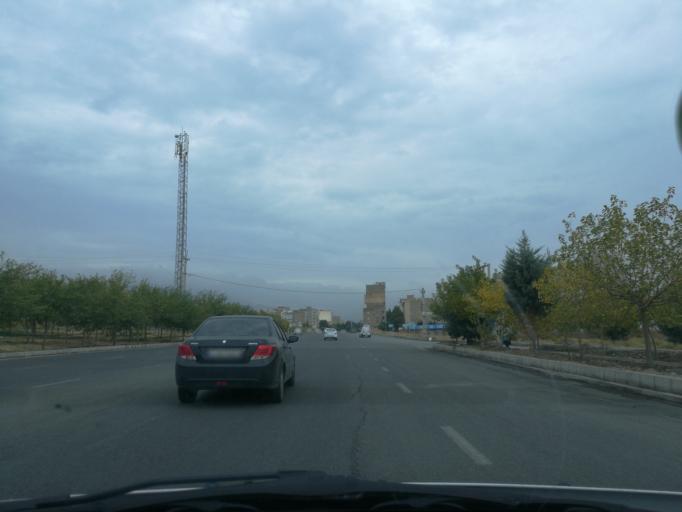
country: IR
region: Alborz
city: Karaj
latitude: 35.8625
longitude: 50.9340
